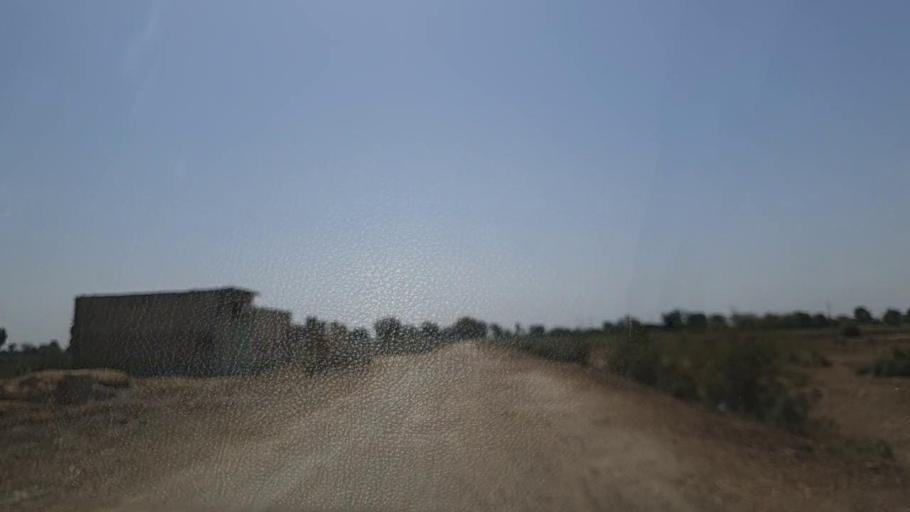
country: PK
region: Sindh
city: Samaro
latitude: 25.2187
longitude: 69.4043
